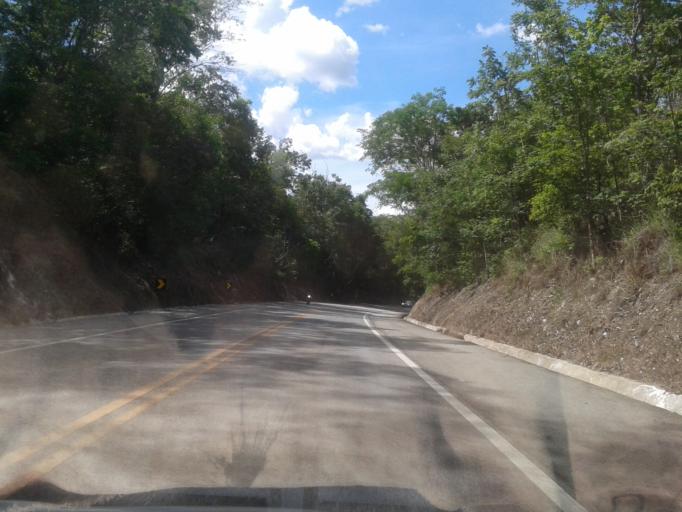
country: BR
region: Goias
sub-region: Goias
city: Goias
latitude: -15.7899
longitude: -50.1312
